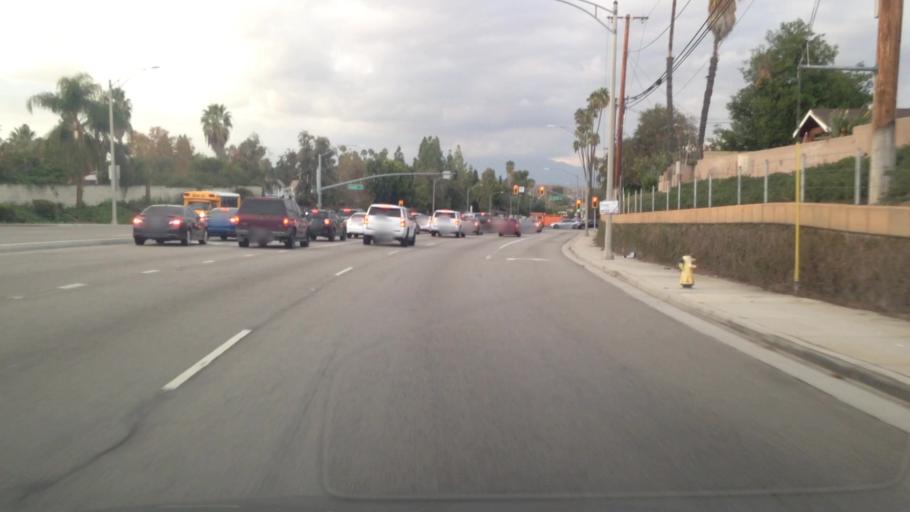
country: US
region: California
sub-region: Riverside County
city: Riverside
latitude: 33.9435
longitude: -117.3538
